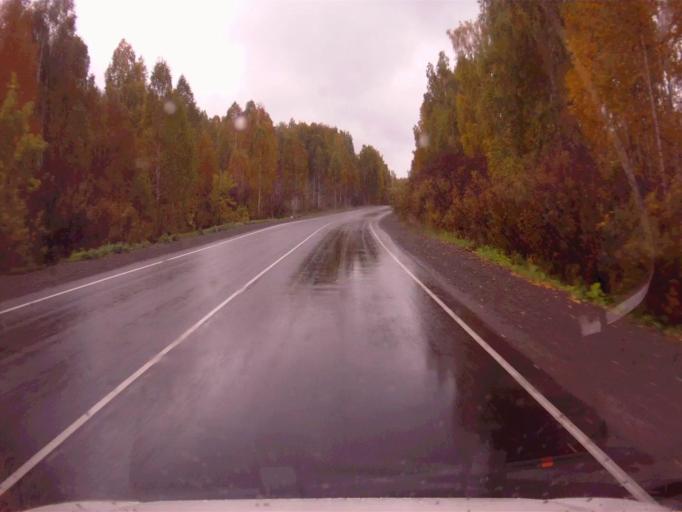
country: RU
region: Chelyabinsk
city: Argayash
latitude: 55.4787
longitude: 60.7620
